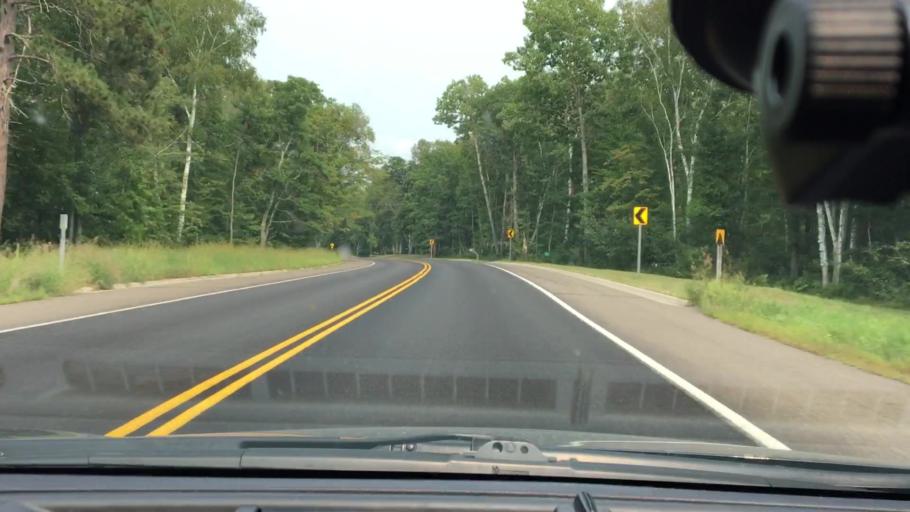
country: US
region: Minnesota
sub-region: Crow Wing County
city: Cross Lake
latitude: 46.7012
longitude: -94.0623
